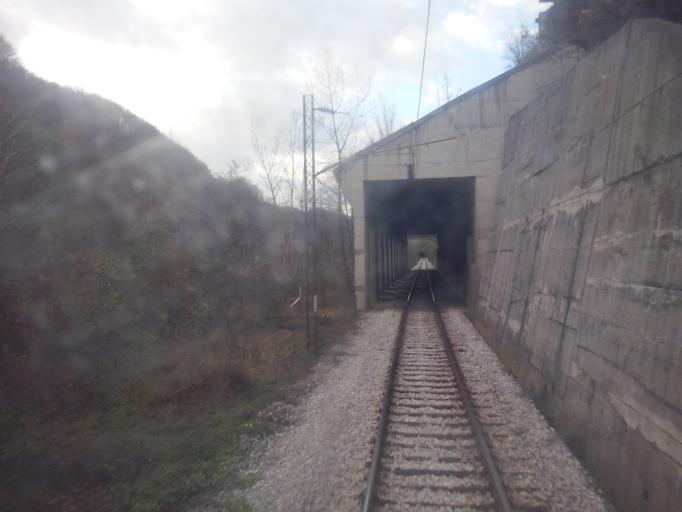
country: RS
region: Central Serbia
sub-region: Zlatiborski Okrug
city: Kosjeric
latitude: 43.9605
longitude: 19.9695
